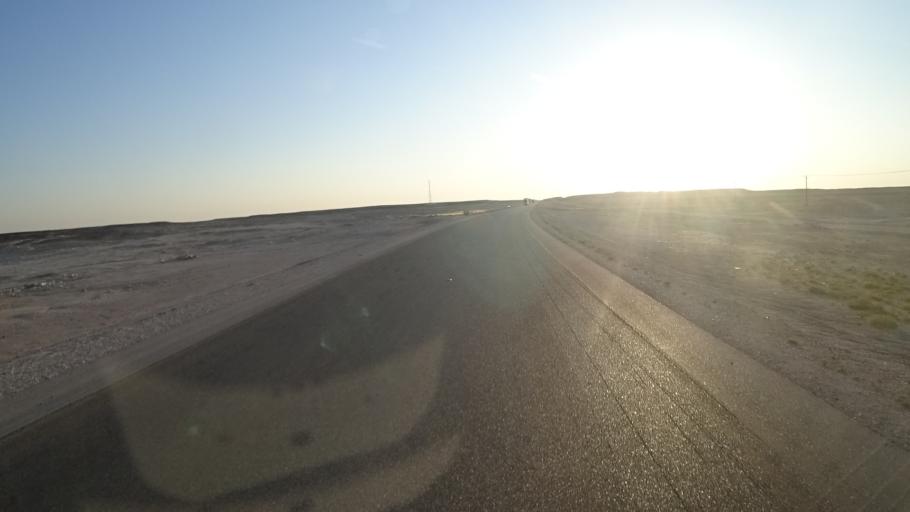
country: OM
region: Zufar
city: Salalah
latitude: 17.5439
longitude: 53.4212
